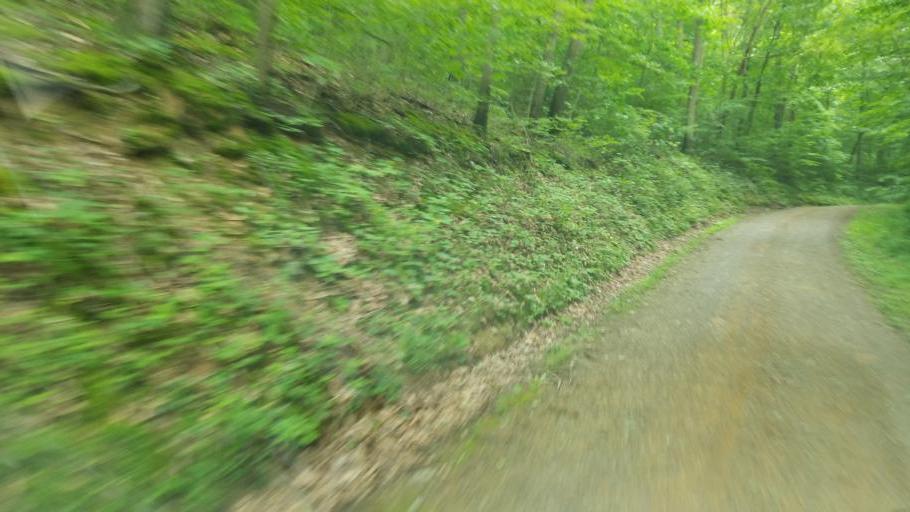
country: US
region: Ohio
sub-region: Columbiana County
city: Salineville
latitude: 40.5529
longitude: -80.8034
